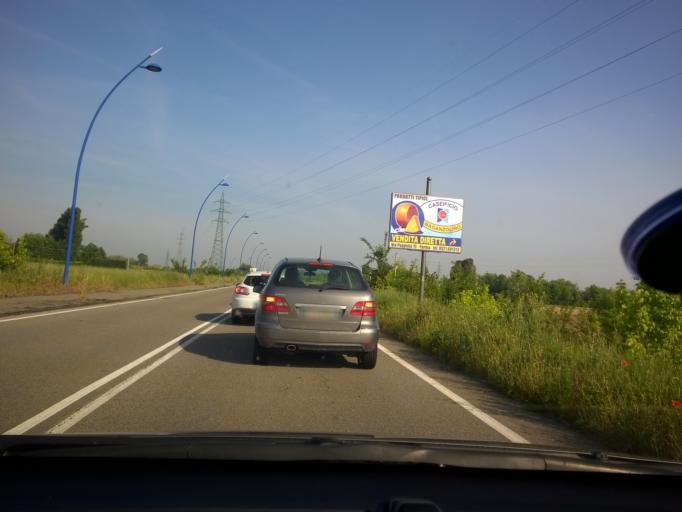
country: IT
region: Emilia-Romagna
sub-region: Provincia di Parma
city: Baganzola
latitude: 44.8401
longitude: 10.3237
